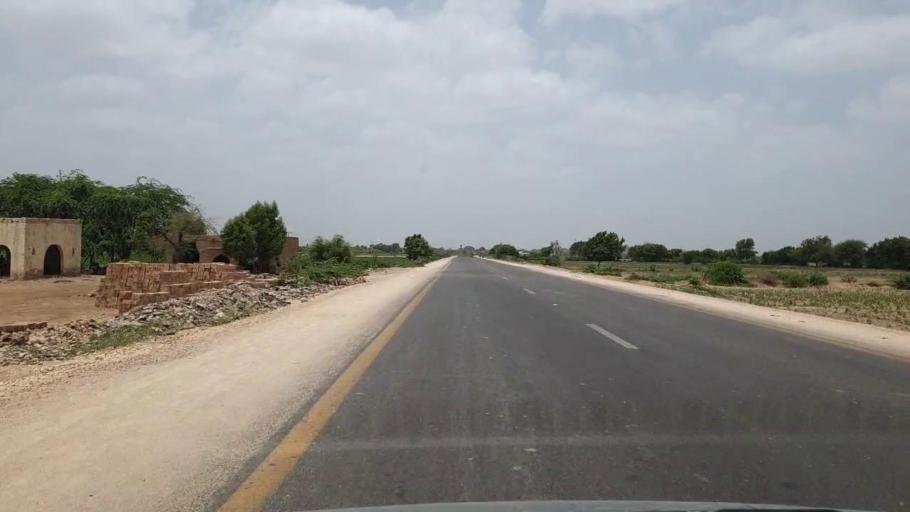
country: PK
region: Sindh
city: Naukot
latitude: 24.8431
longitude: 69.4340
